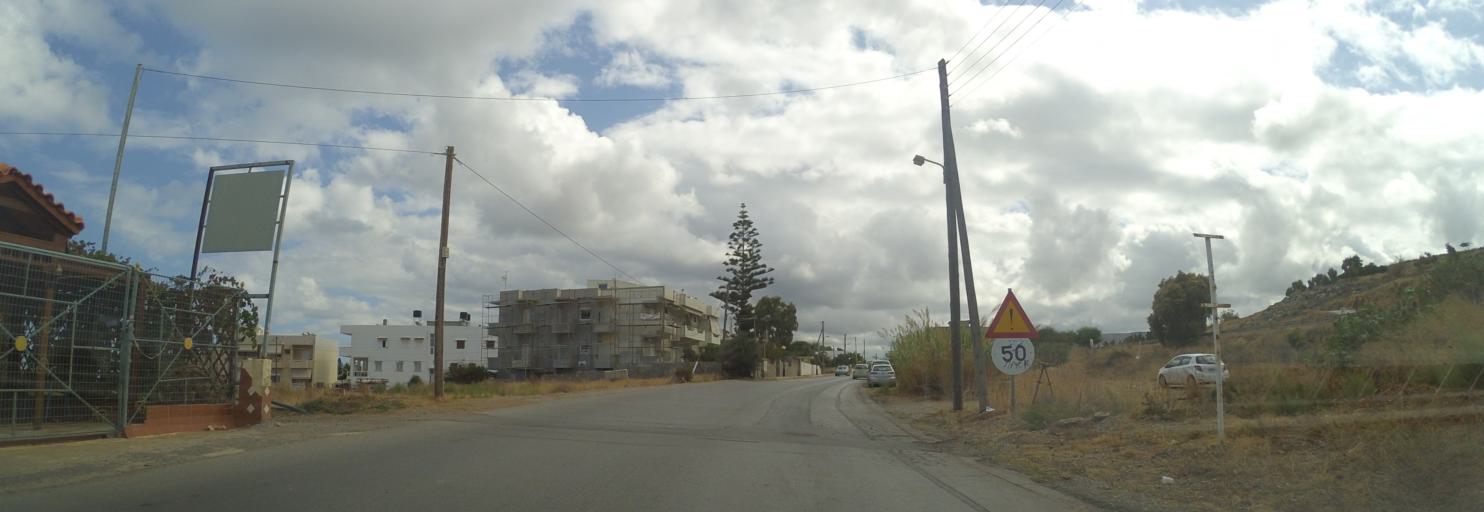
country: GR
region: Crete
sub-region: Nomos Irakleiou
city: Gournes
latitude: 35.3283
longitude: 25.2721
